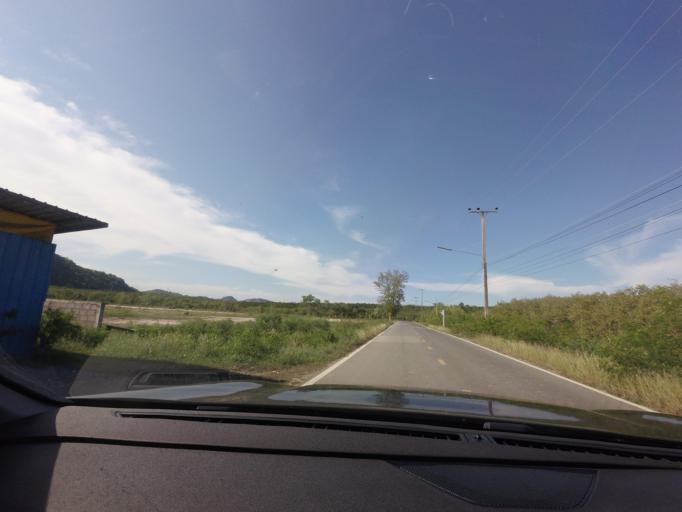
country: TH
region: Prachuap Khiri Khan
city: Pran Buri
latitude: 12.4074
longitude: 99.9833
